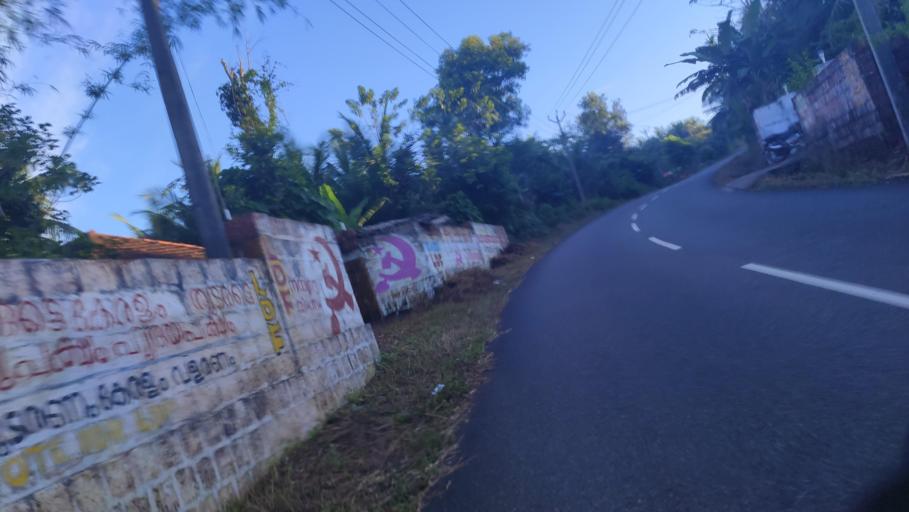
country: IN
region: Kerala
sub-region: Kasaragod District
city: Kasaragod
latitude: 12.4501
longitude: 75.0996
